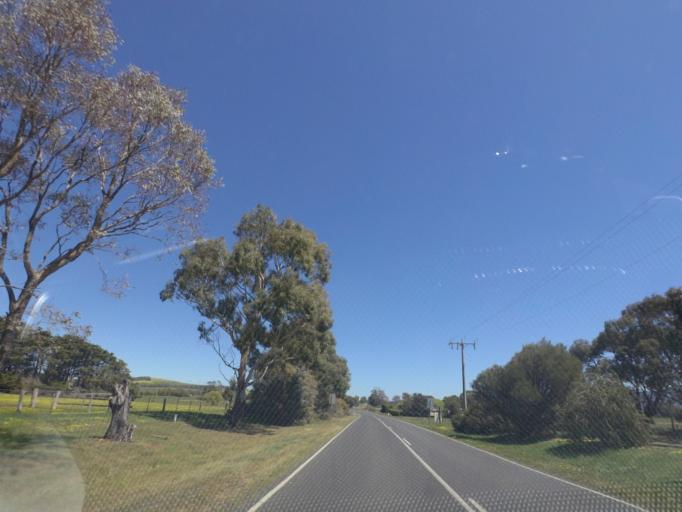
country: AU
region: Victoria
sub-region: Hume
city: Sunbury
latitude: -37.2792
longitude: 144.7170
